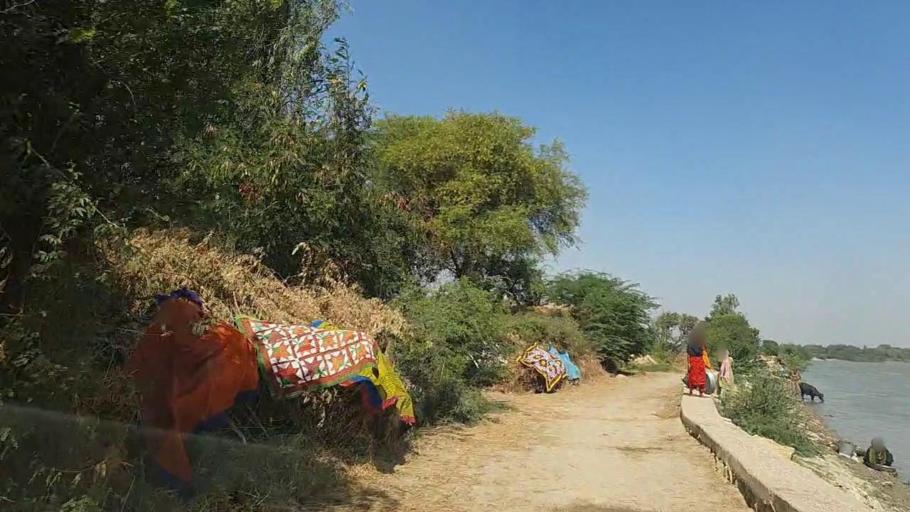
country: PK
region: Sindh
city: Daro Mehar
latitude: 24.8167
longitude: 68.1872
